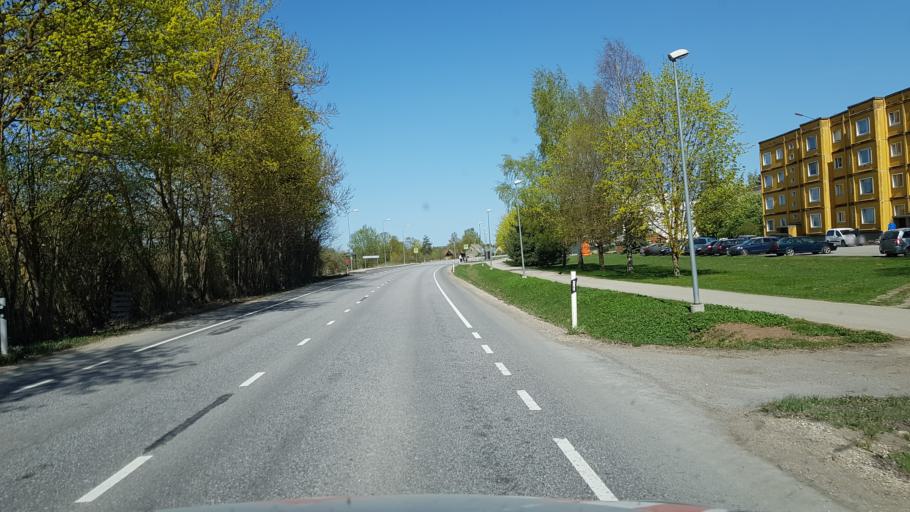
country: EE
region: Tartu
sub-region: Puhja vald
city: Puhja
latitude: 58.3337
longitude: 26.3052
